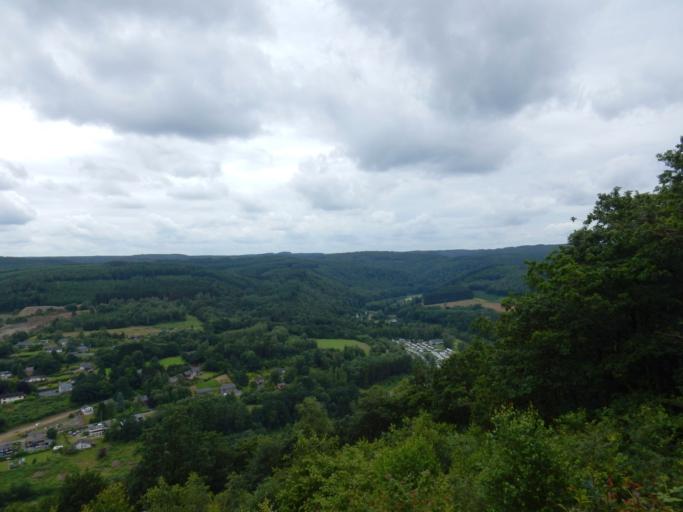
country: BE
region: Wallonia
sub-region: Province de Namur
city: Bievre
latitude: 49.8586
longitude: 4.9652
